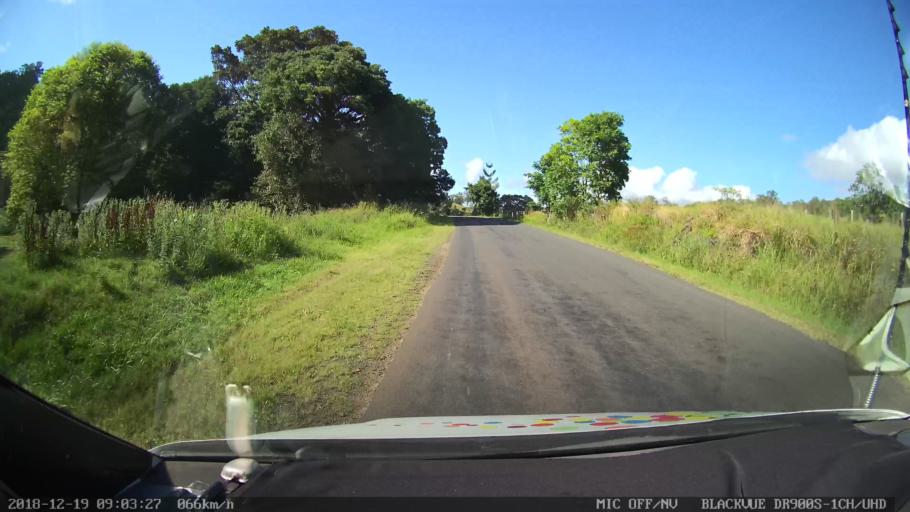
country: AU
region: New South Wales
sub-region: Kyogle
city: Kyogle
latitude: -28.4477
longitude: 152.9508
